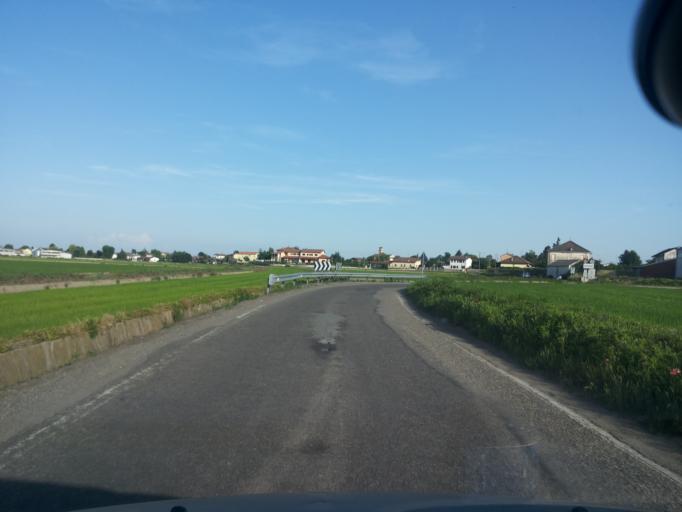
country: IT
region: Piedmont
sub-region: Provincia di Vercelli
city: Pezzana
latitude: 45.2665
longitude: 8.4759
